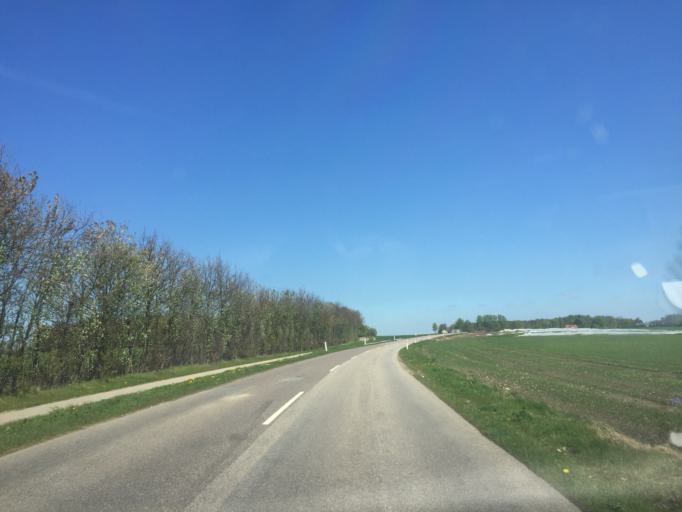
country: DK
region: Capital Region
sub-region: Egedal Kommune
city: Vekso
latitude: 55.7781
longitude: 12.2376
